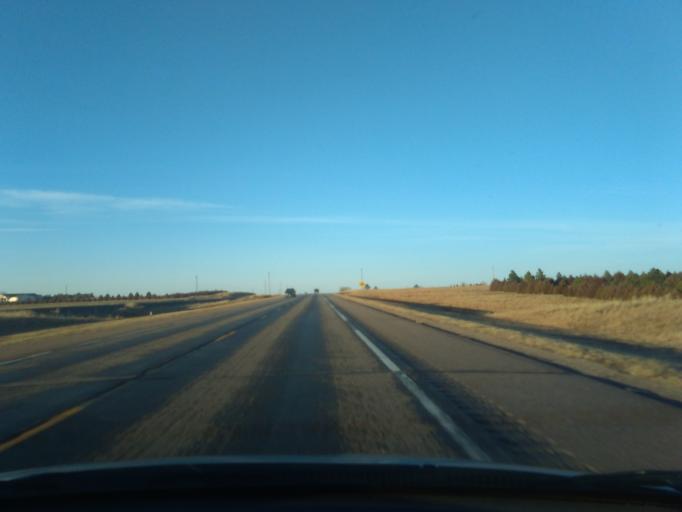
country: US
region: Nebraska
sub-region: Cheyenne County
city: Sidney
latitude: 41.1898
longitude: -102.9680
